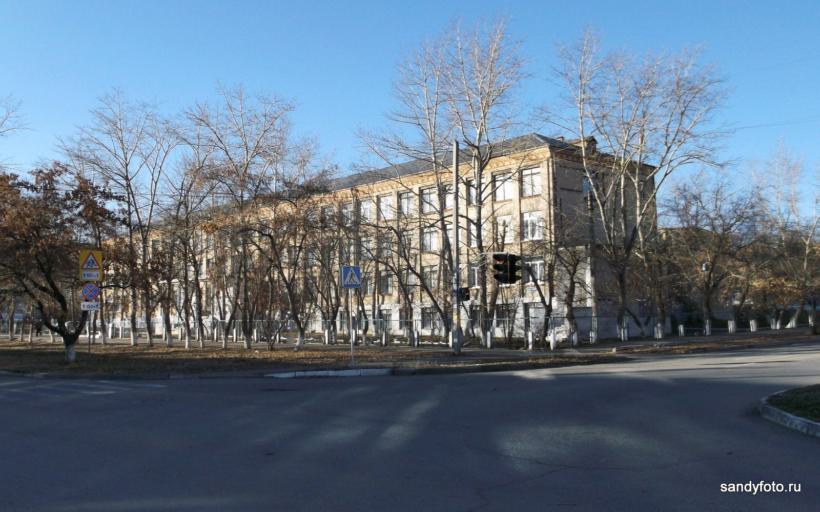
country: RU
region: Chelyabinsk
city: Troitsk
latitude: 54.0793
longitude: 61.5373
